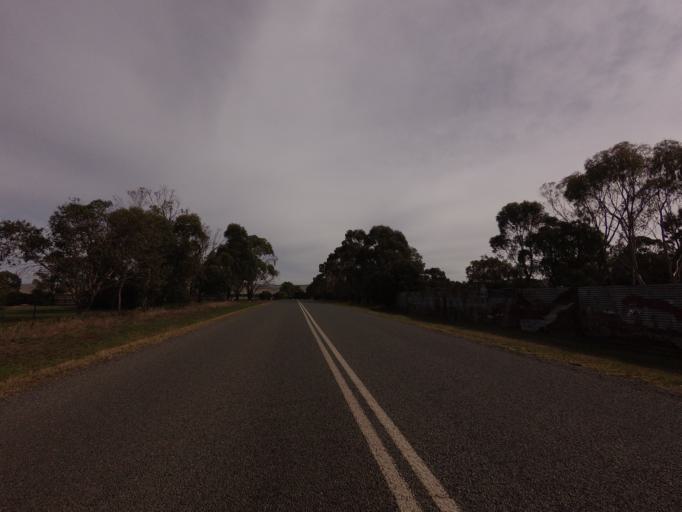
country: AU
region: Tasmania
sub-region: Brighton
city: Bridgewater
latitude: -42.3078
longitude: 147.3649
